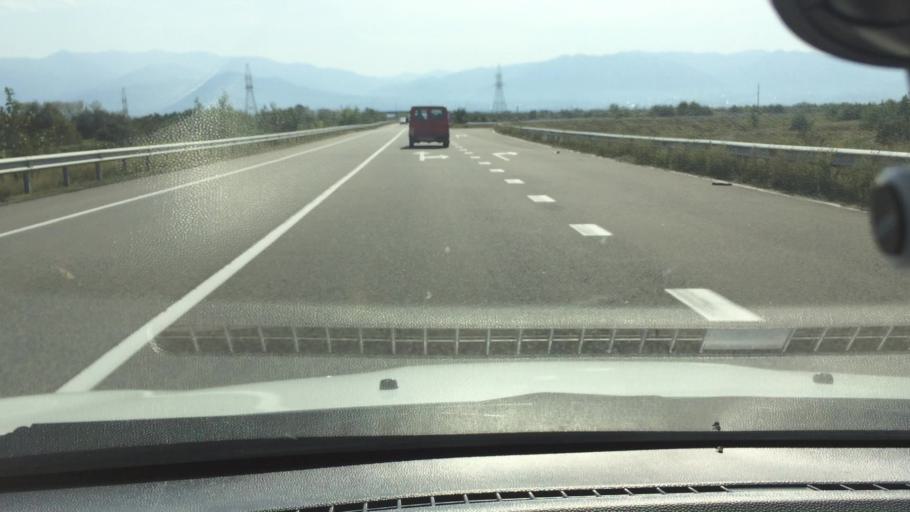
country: GE
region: Ajaria
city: Ochkhamuri
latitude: 41.9032
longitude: 41.7915
